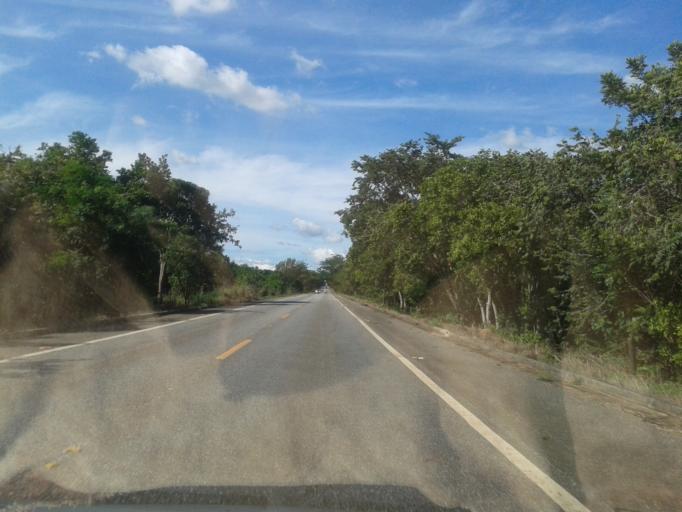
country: BR
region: Goias
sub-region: Mozarlandia
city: Mozarlandia
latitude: -14.9618
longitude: -50.5795
